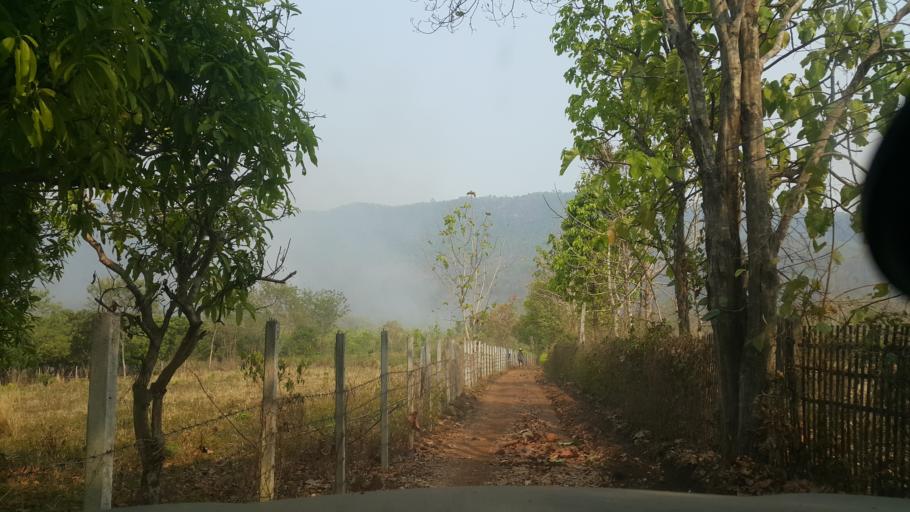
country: TH
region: Chiang Mai
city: Mae On
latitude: 18.7604
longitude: 99.2698
